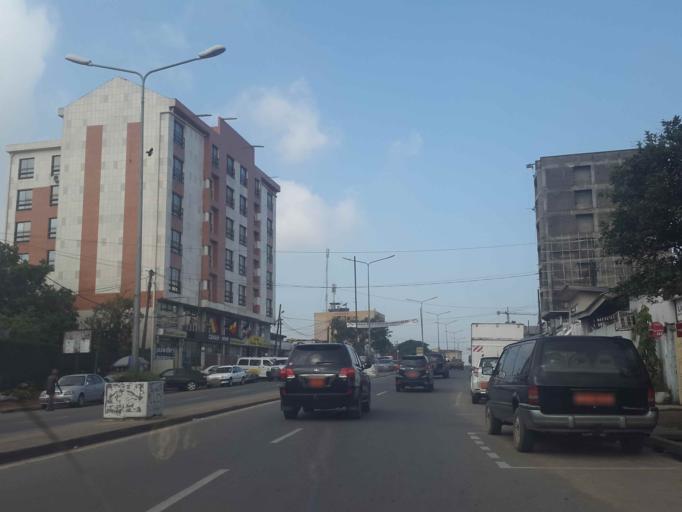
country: CM
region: Littoral
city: Douala
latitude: 4.0430
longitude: 9.6961
